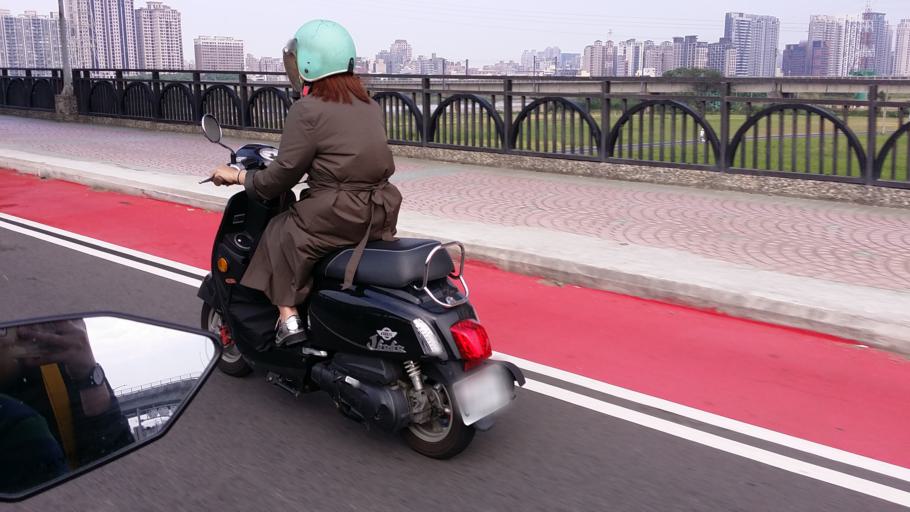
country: TW
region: Taiwan
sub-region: Hsinchu
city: Zhubei
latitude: 24.8204
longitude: 120.9961
